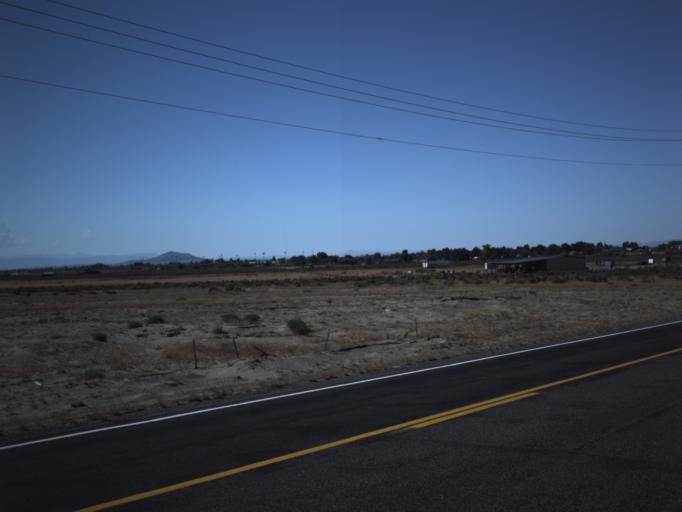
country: US
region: Utah
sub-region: Millard County
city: Delta
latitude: 39.3625
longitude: -112.5517
